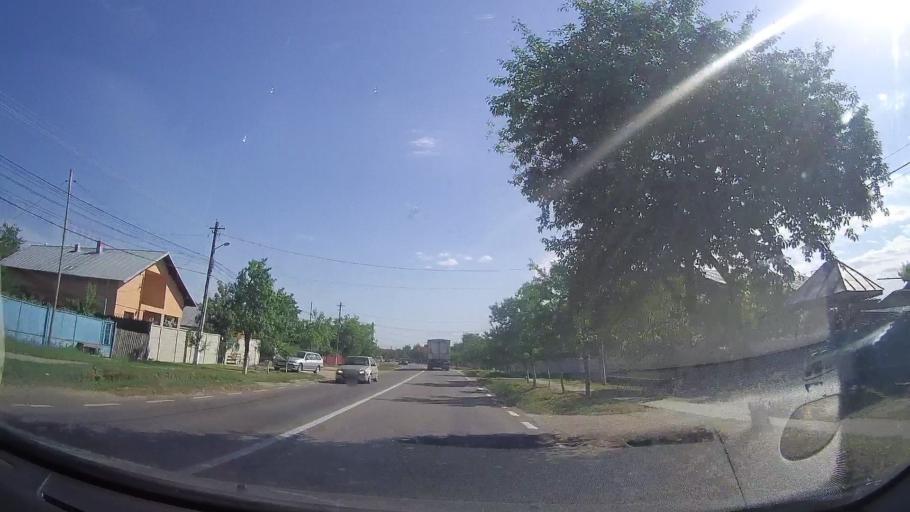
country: RO
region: Prahova
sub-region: Comuna Gura Vitioarei
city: Fagetu
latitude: 45.1216
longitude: 26.0342
